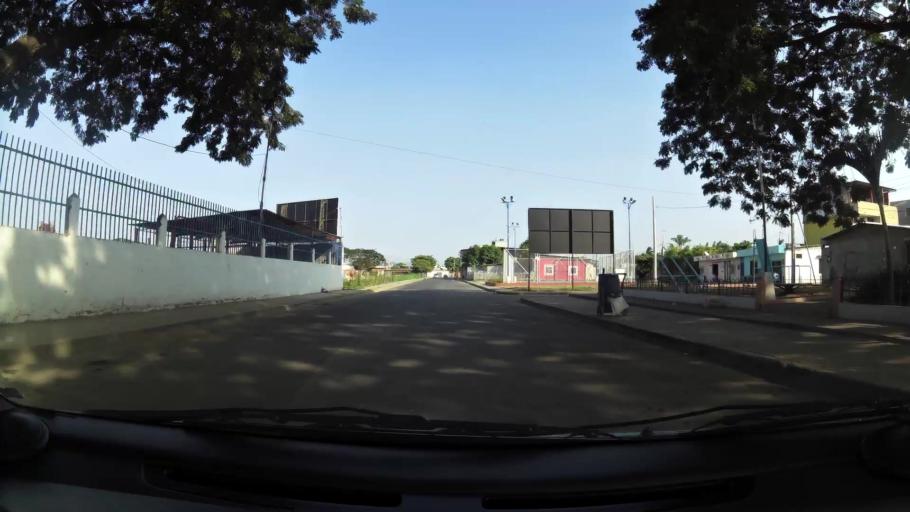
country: EC
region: Guayas
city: Eloy Alfaro
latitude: -2.1861
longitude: -79.8476
